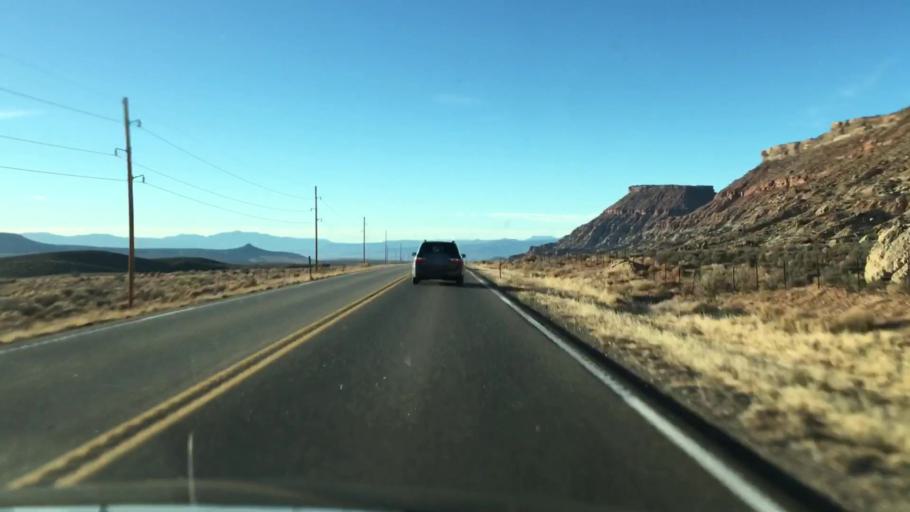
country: US
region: Utah
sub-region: Washington County
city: LaVerkin
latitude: 37.1223
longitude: -113.1903
